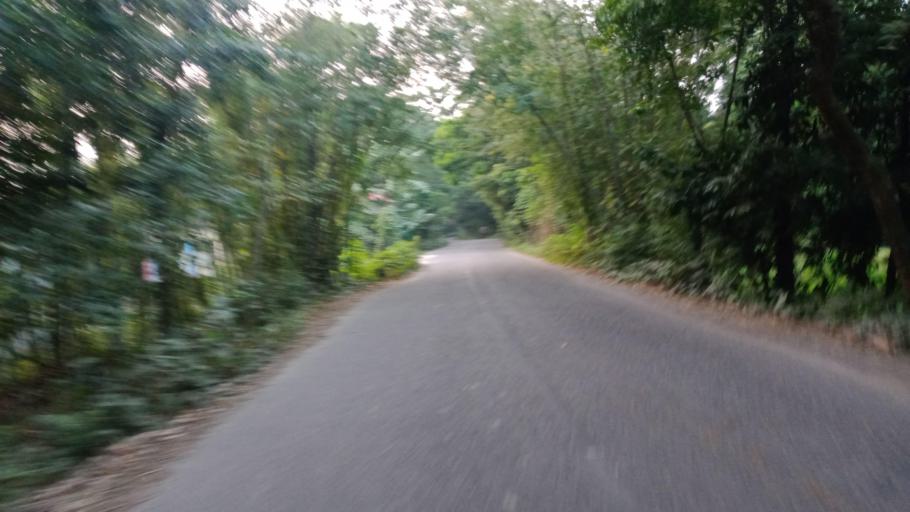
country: BD
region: Chittagong
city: Hajiganj
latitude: 23.3695
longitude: 90.9837
